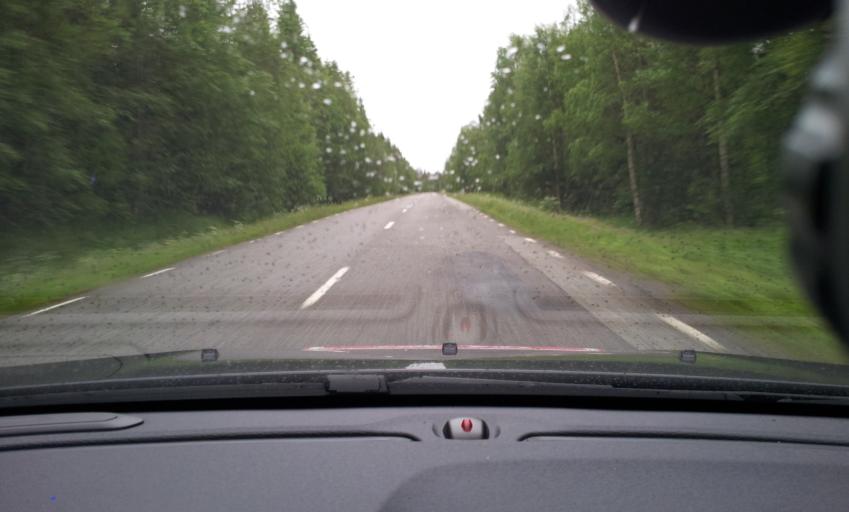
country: SE
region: Jaemtland
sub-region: Ragunda Kommun
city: Hammarstrand
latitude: 63.2364
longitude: 15.9188
